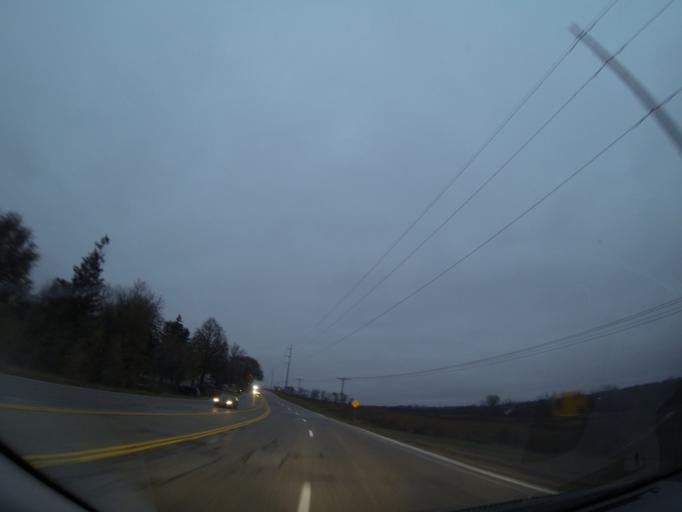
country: US
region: Nebraska
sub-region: Douglas County
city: Elkhorn
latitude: 41.2665
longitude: -96.1772
